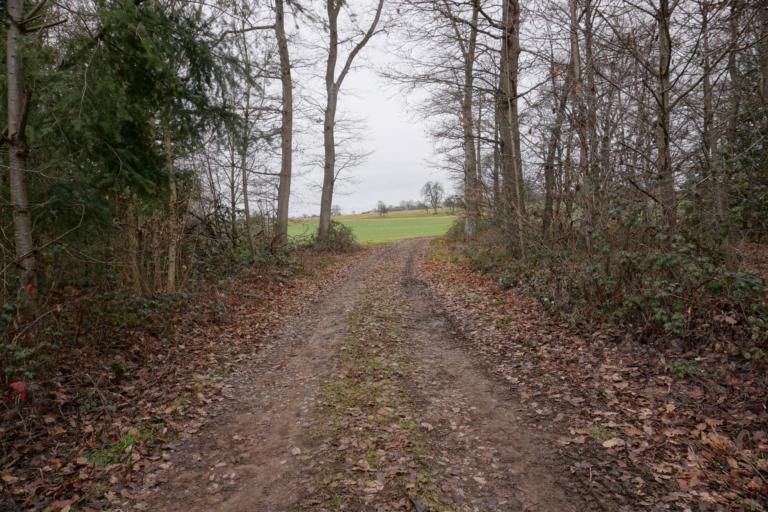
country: DE
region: Baden-Wuerttemberg
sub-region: Karlsruhe Region
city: Neckargerach
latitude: 49.4249
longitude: 9.0897
